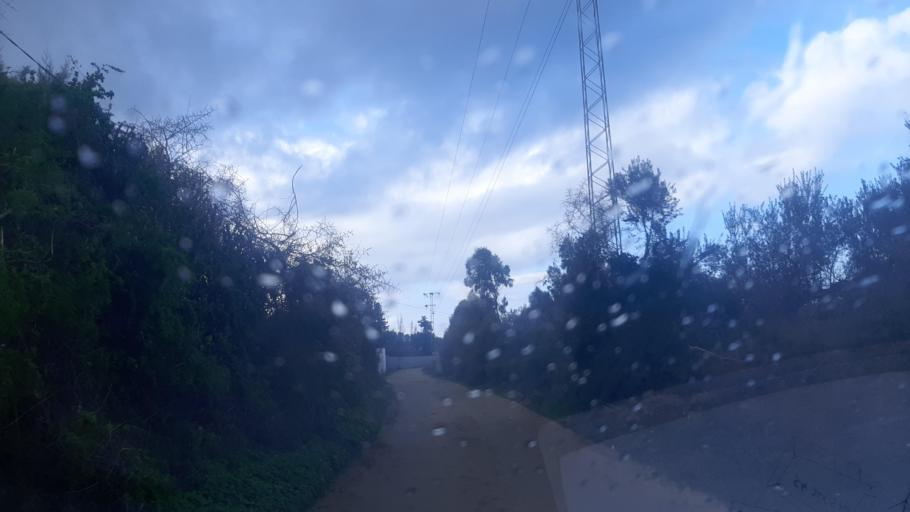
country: TN
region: Nabul
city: Manzil Bu Zalafah
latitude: 36.7415
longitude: 10.5283
